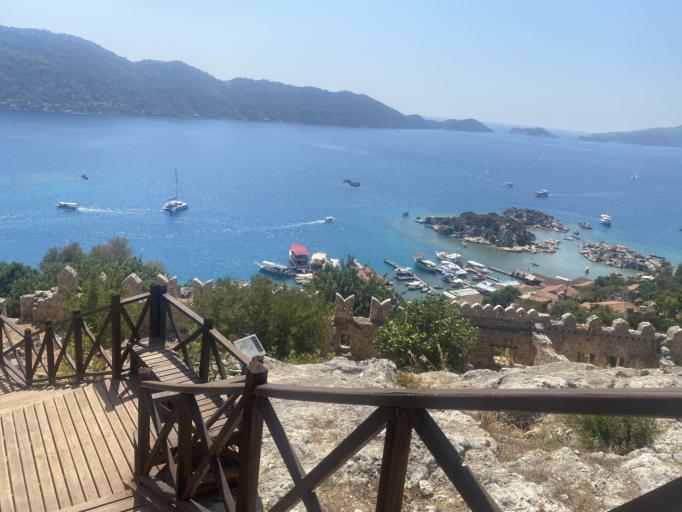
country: TR
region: Antalya
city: Demre
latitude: 36.1913
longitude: 29.8623
